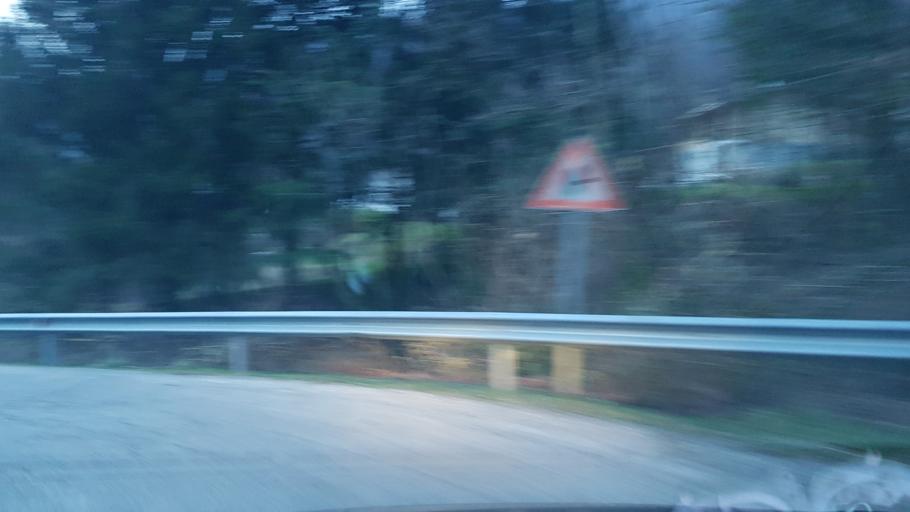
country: IT
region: Friuli Venezia Giulia
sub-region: Provincia di Udine
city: Attimis
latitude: 46.1956
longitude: 13.3314
